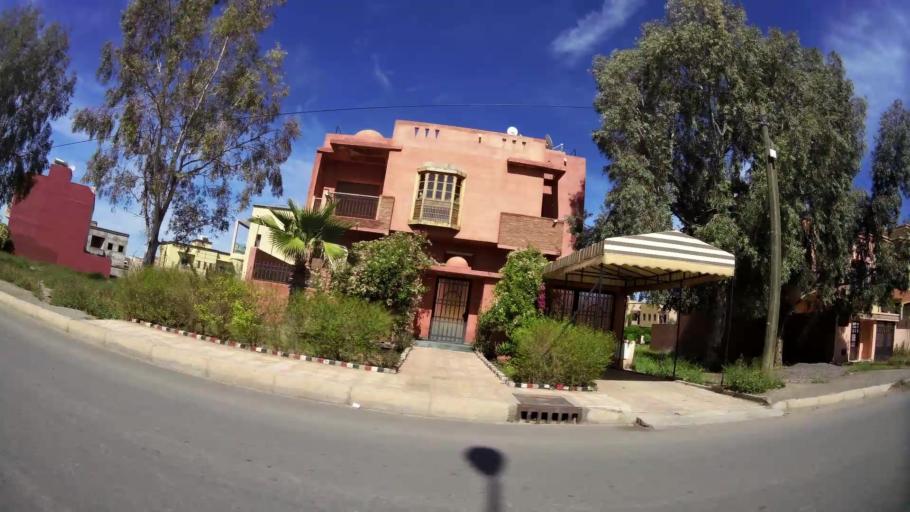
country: MA
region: Marrakech-Tensift-Al Haouz
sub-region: Marrakech
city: Marrakesh
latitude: 31.6432
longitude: -8.0430
